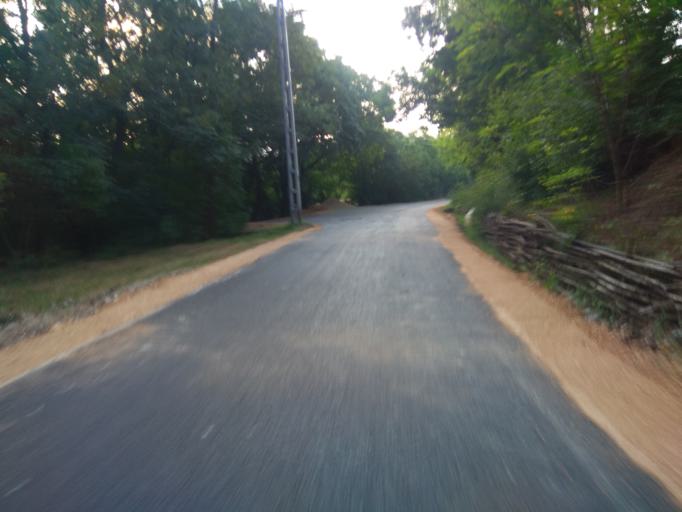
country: HU
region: Borsod-Abauj-Zemplen
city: Harsany
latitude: 47.9844
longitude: 20.7881
